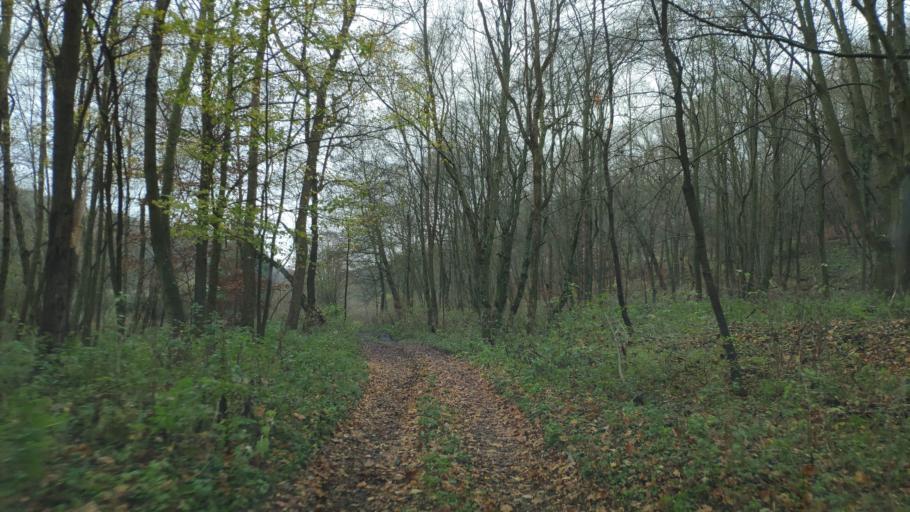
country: SK
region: Presovsky
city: Sabinov
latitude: 49.1414
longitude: 21.2152
